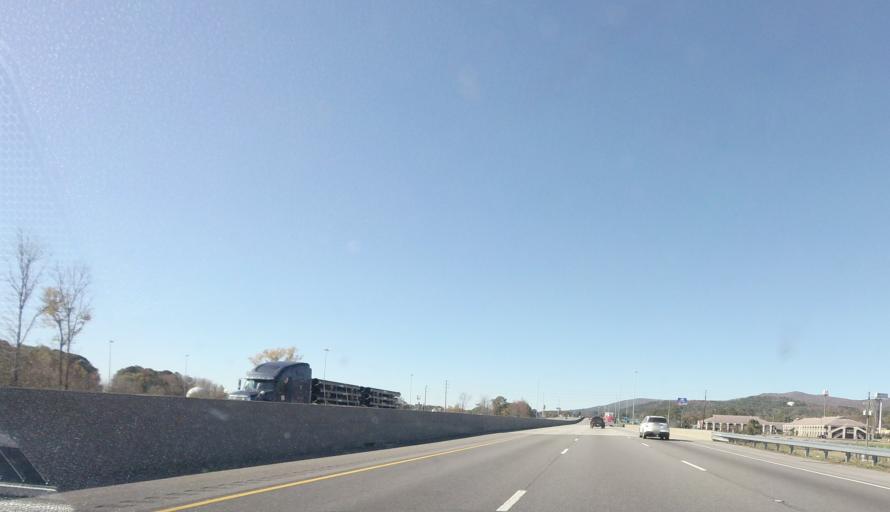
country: US
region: Alabama
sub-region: Calhoun County
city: Oxford
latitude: 33.6051
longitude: -85.8240
